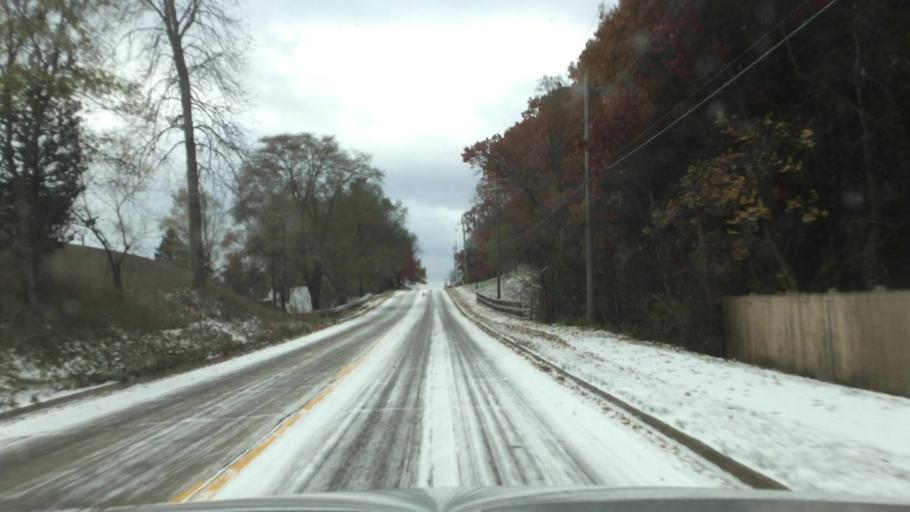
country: US
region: Michigan
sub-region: Livingston County
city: Brighton
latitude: 42.5399
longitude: -83.8131
